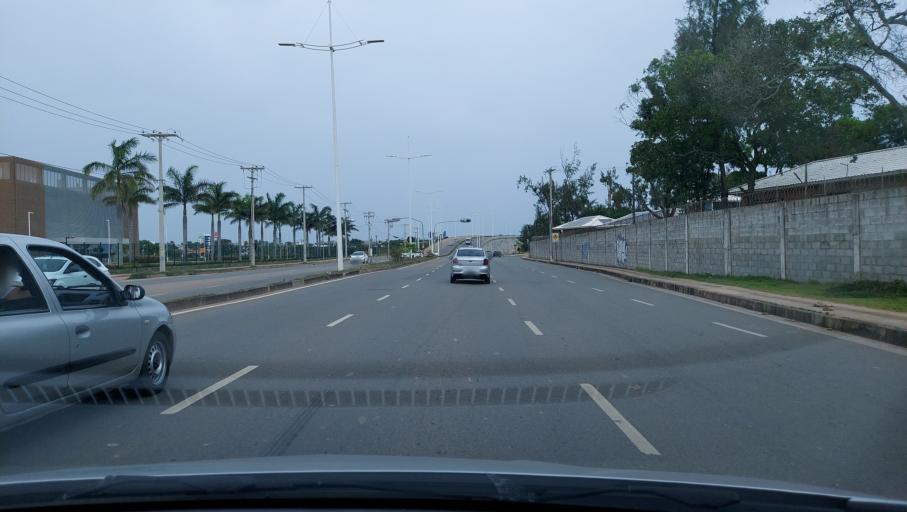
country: BR
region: Bahia
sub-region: Lauro De Freitas
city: Lauro de Freitas
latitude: -12.9448
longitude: -38.3851
